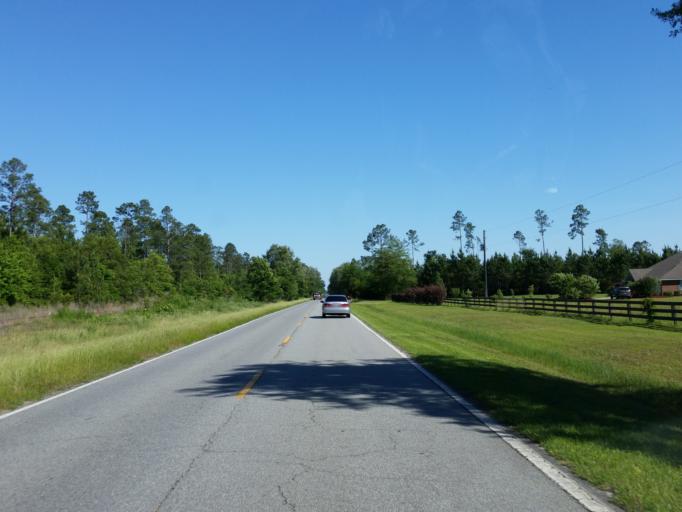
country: US
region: Georgia
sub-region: Echols County
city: Statenville
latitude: 30.6574
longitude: -83.1522
